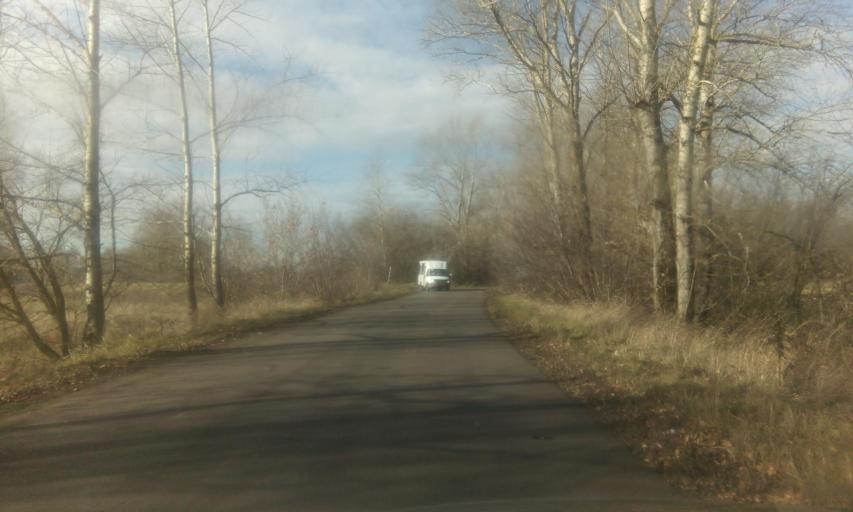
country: RU
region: Tula
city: Dubovka
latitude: 53.9580
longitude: 38.0542
